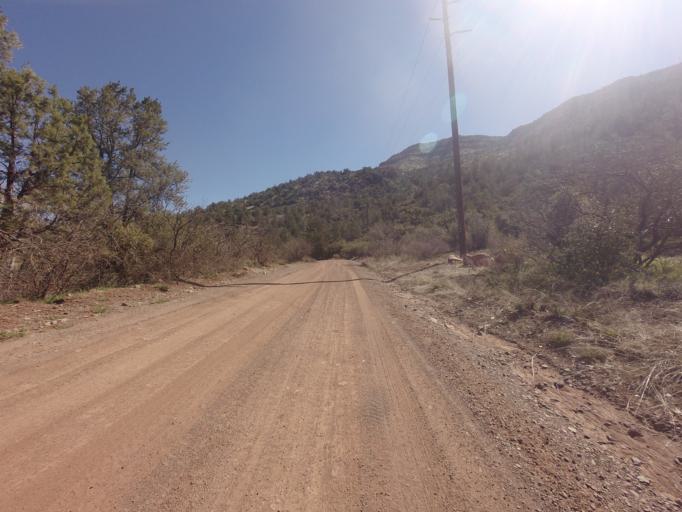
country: US
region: Arizona
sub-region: Gila County
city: Pine
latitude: 34.4003
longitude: -111.6192
